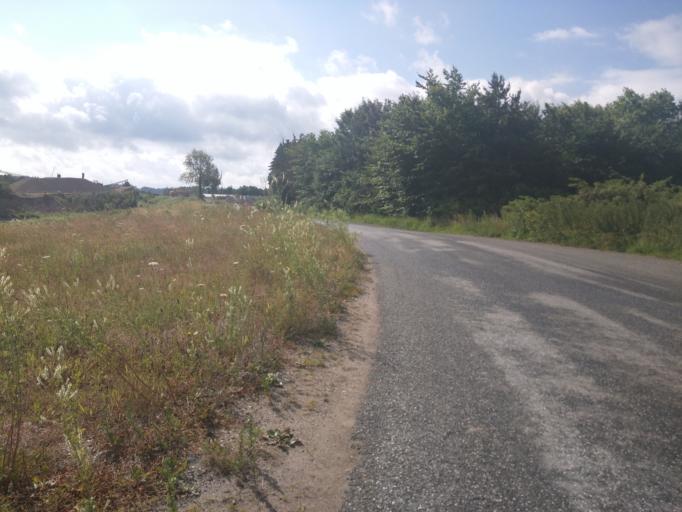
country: DK
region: Zealand
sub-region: Kalundborg Kommune
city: Svebolle
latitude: 55.6731
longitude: 11.3110
